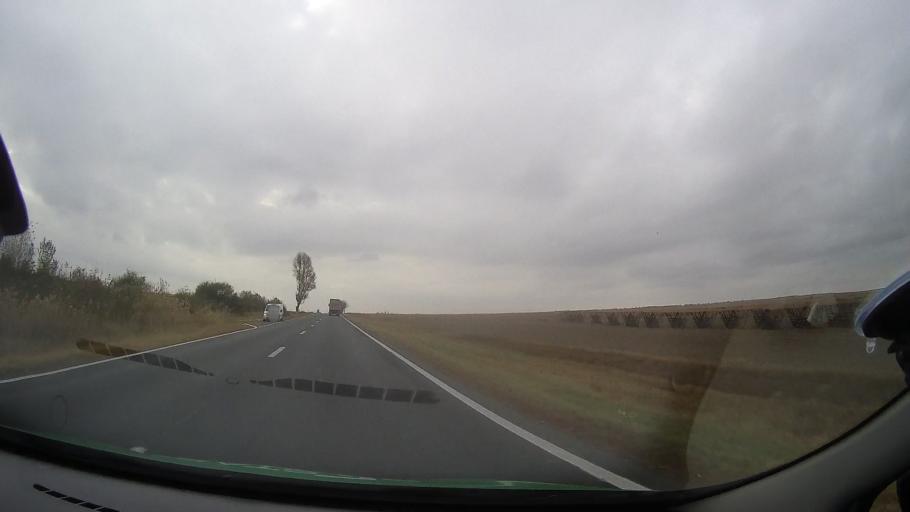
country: RO
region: Constanta
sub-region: Comuna Castelu
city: Castelu
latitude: 44.2535
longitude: 28.3189
